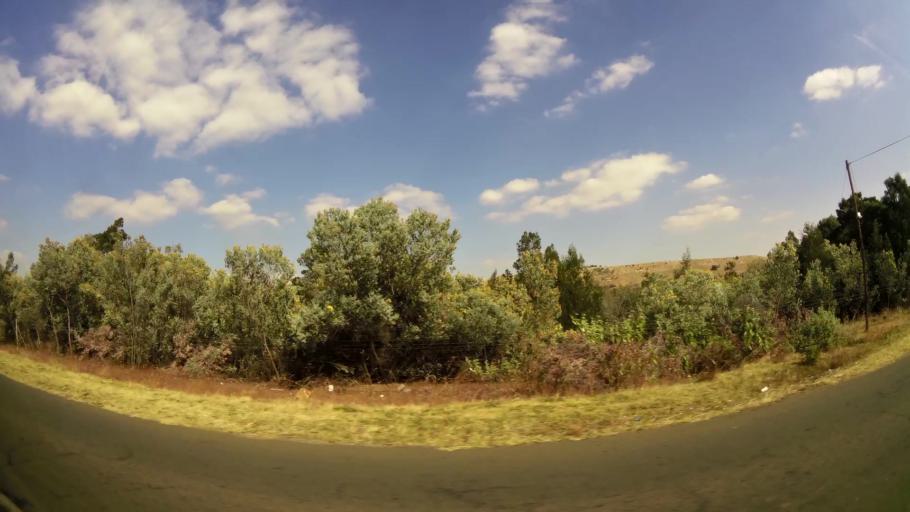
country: ZA
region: Gauteng
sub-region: West Rand District Municipality
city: Krugersdorp
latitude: -26.0450
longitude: 27.7500
